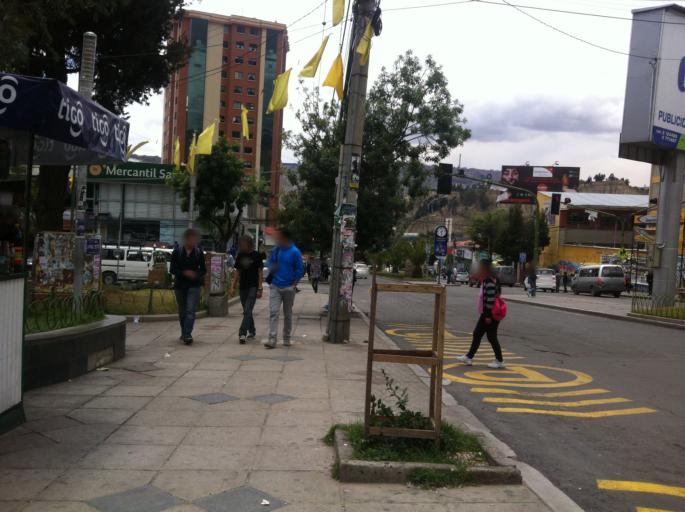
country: BO
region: La Paz
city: La Paz
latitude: -16.5390
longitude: -68.0777
